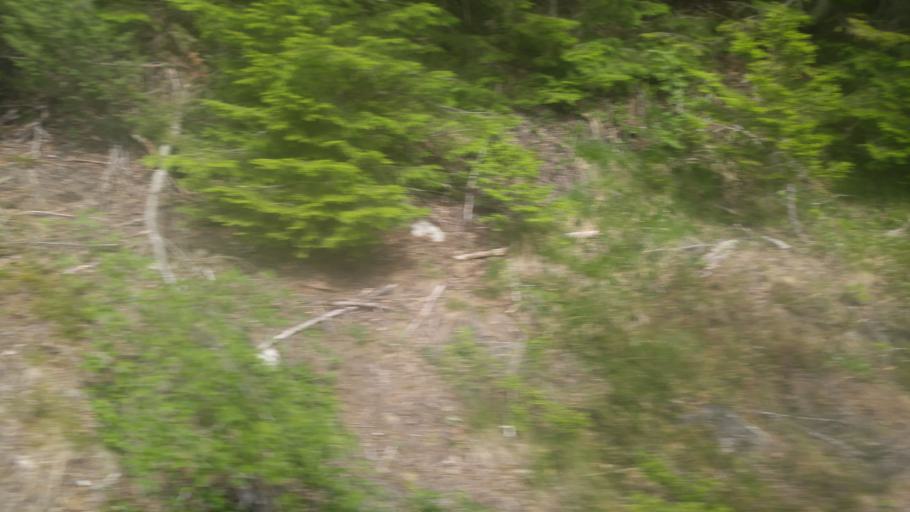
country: NO
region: Sor-Trondelag
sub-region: Selbu
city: Mebonden
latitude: 62.9598
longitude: 10.8492
